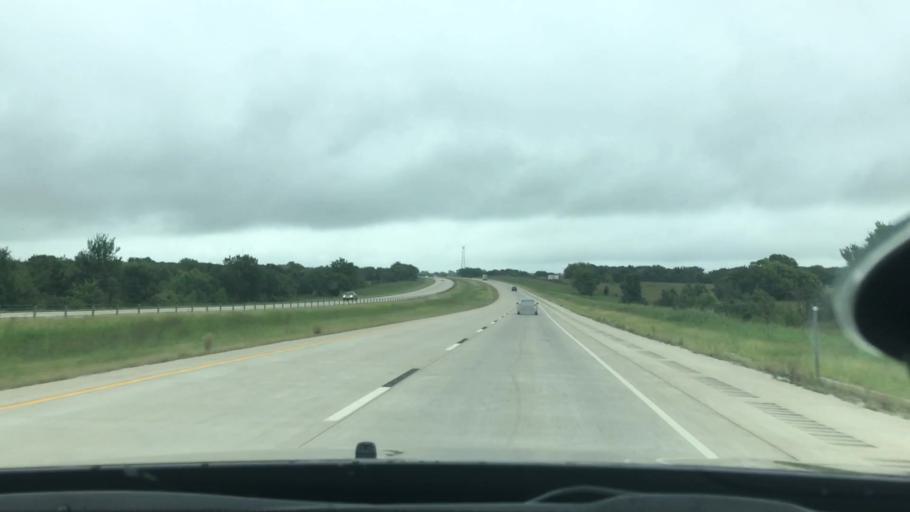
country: US
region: Oklahoma
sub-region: Okmulgee County
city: Wilson
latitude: 35.4274
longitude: -96.0702
